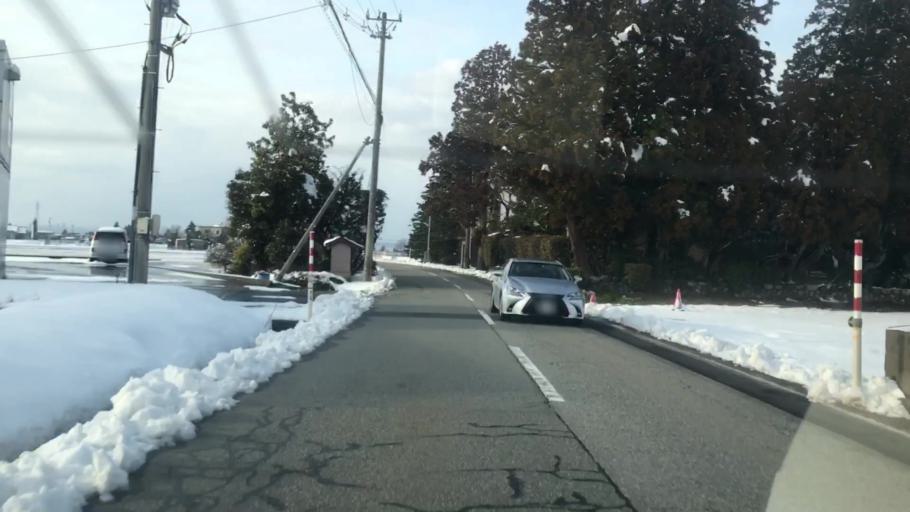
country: JP
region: Toyama
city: Toyama-shi
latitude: 36.6378
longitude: 137.2626
